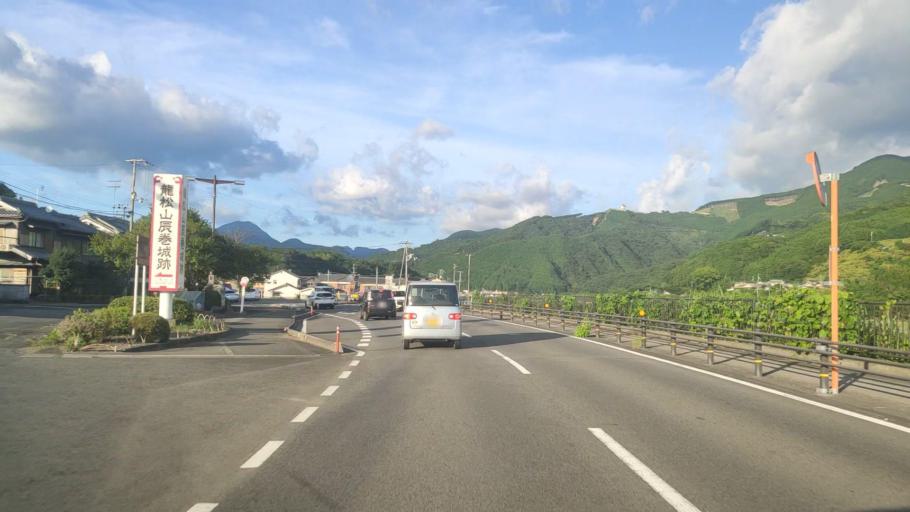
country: JP
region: Wakayama
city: Tanabe
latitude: 33.7164
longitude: 135.4705
